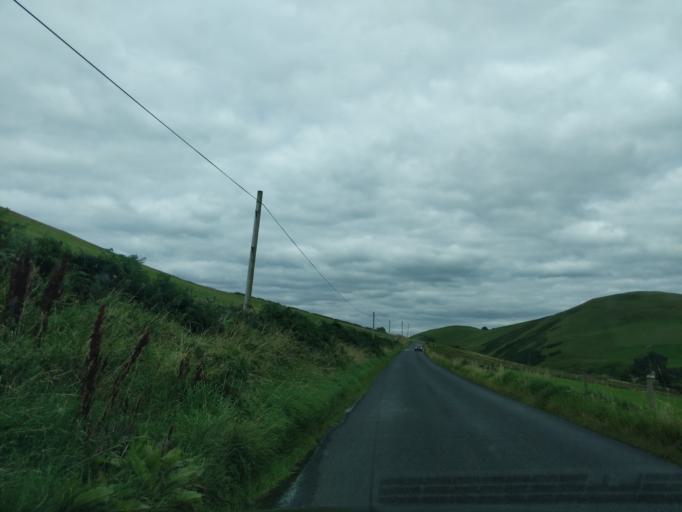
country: GB
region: Scotland
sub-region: The Scottish Borders
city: West Linton
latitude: 55.6877
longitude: -3.3339
